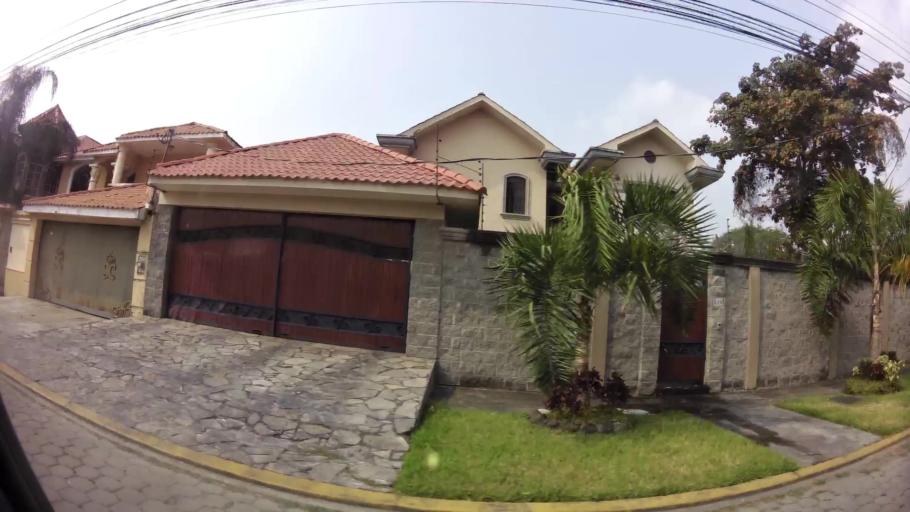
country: HN
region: Cortes
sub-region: San Pedro Sula
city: Pena Blanca
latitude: 15.5366
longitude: -88.0237
